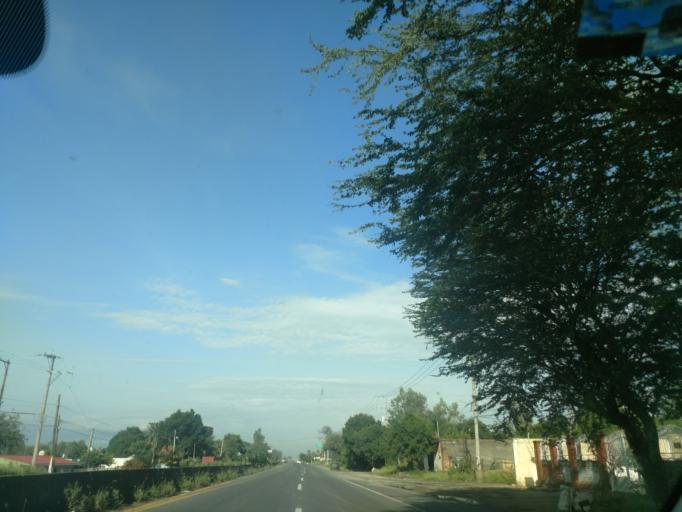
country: MX
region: Jalisco
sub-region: Ameca
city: Los Pocitos
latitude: 20.5368
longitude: -103.9397
